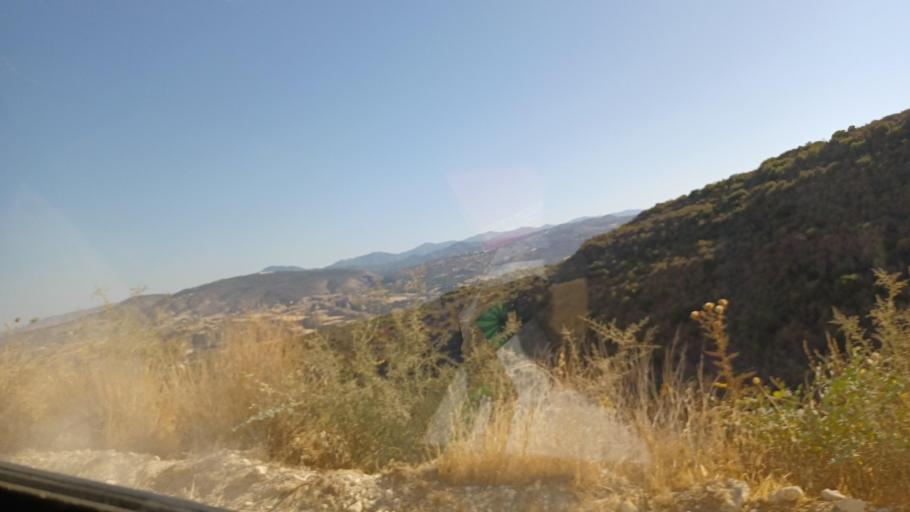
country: CY
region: Pafos
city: Polis
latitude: 34.9652
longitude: 32.4358
